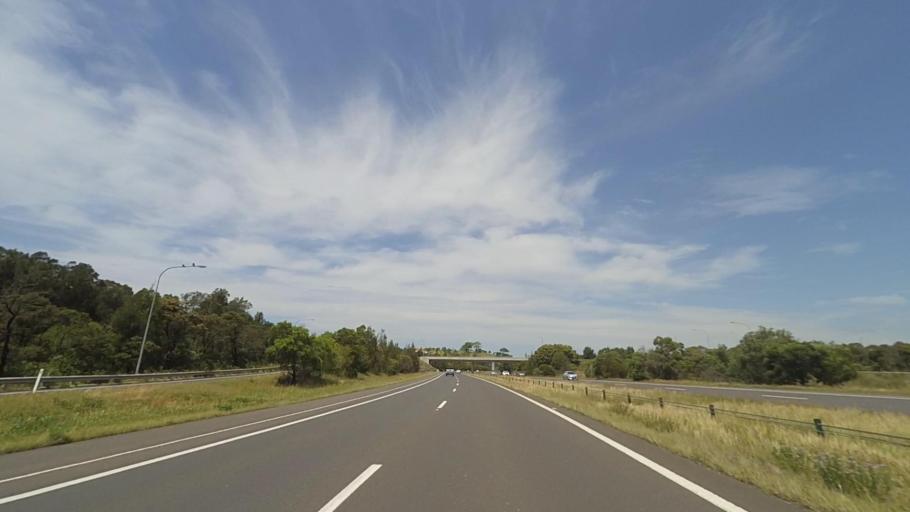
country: AU
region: New South Wales
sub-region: Shellharbour
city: Croom
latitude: -34.6146
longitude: 150.8373
